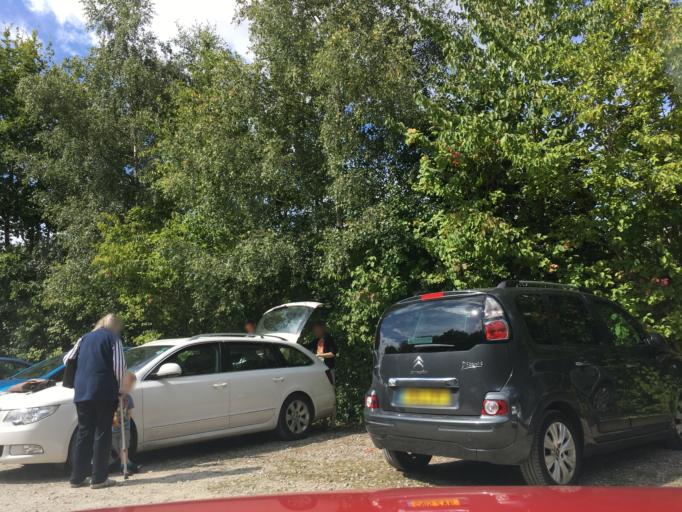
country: GB
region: England
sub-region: Kent
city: Cranbrook
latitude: 51.1169
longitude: 0.5773
